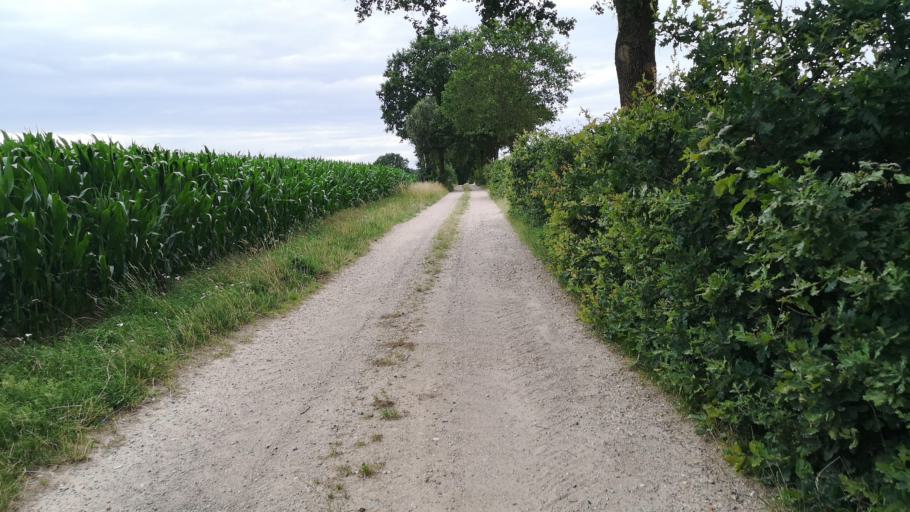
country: DE
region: Lower Saxony
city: Dahlenburg
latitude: 53.2042
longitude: 10.7052
